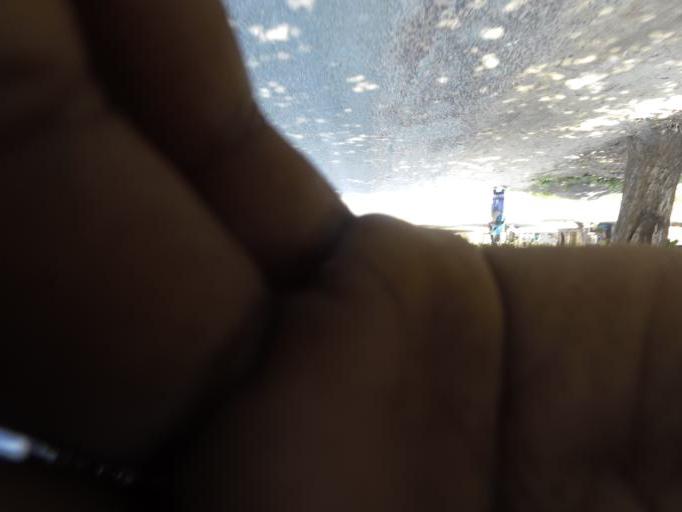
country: TZ
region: Pwani
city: Vikindu
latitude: -7.0332
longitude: 39.2769
